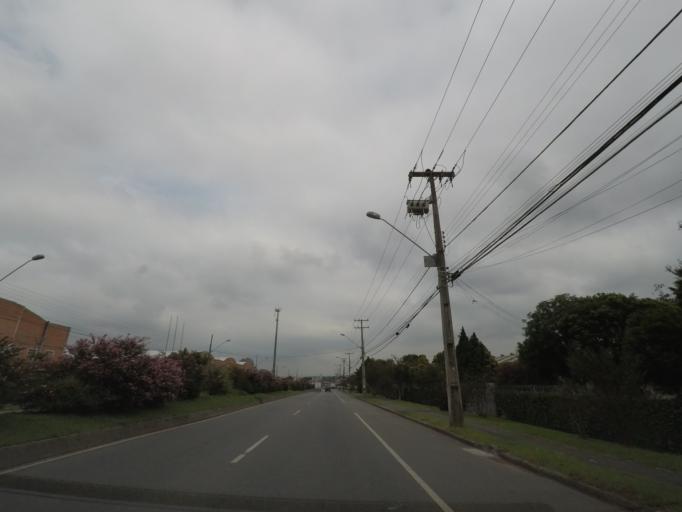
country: BR
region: Parana
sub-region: Curitiba
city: Curitiba
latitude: -25.5095
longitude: -49.3308
